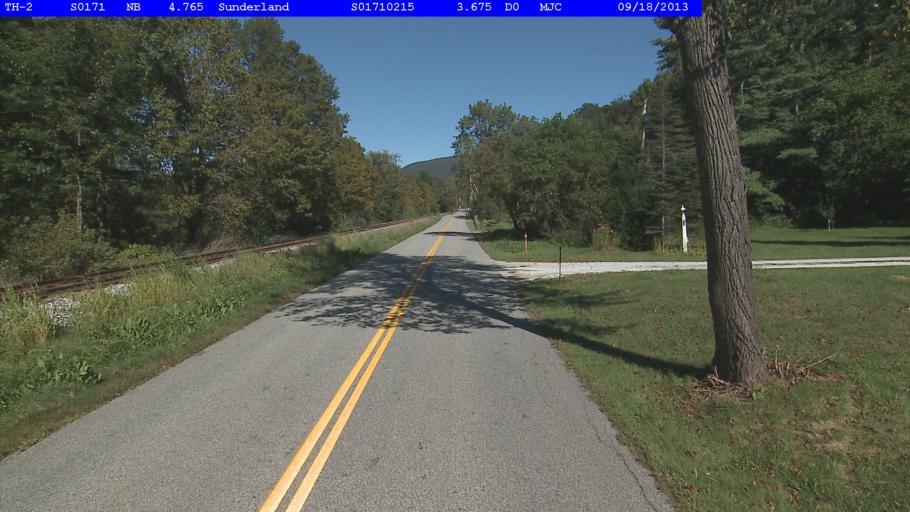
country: US
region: Vermont
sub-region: Bennington County
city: Arlington
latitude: 43.1118
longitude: -73.1090
